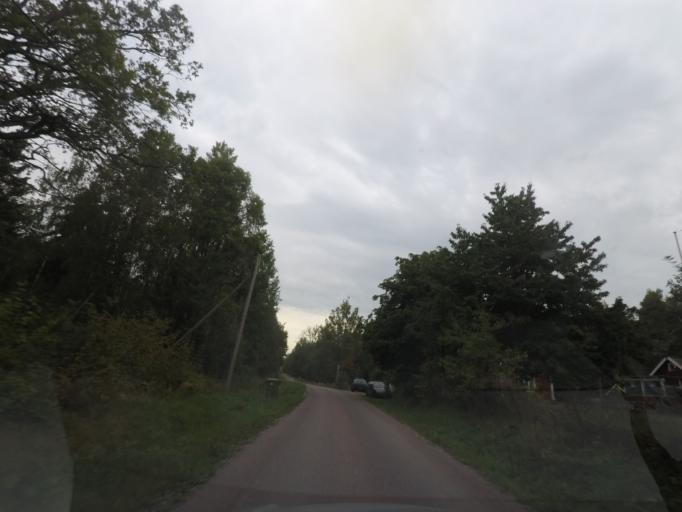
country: SE
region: Vaestmanland
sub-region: Hallstahammars Kommun
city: Kolback
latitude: 59.4920
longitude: 16.1931
